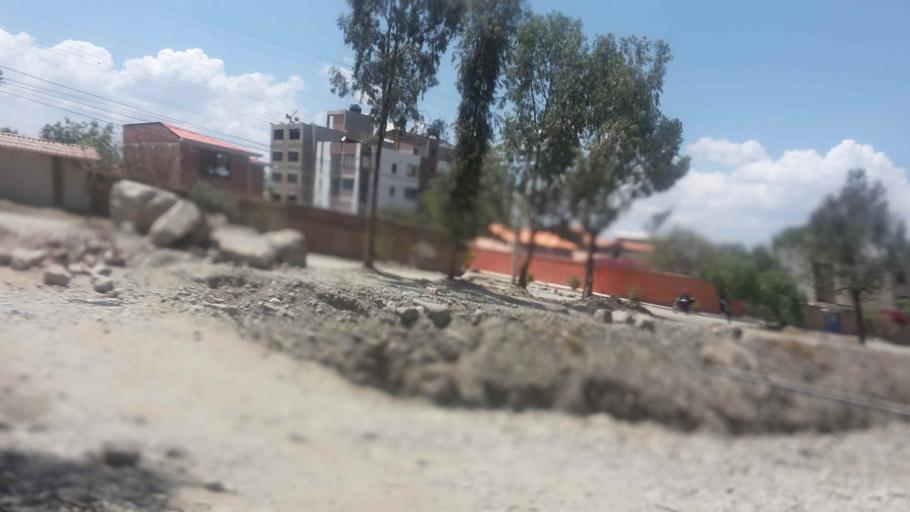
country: BO
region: Cochabamba
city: Cochabamba
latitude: -17.3475
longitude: -66.2001
